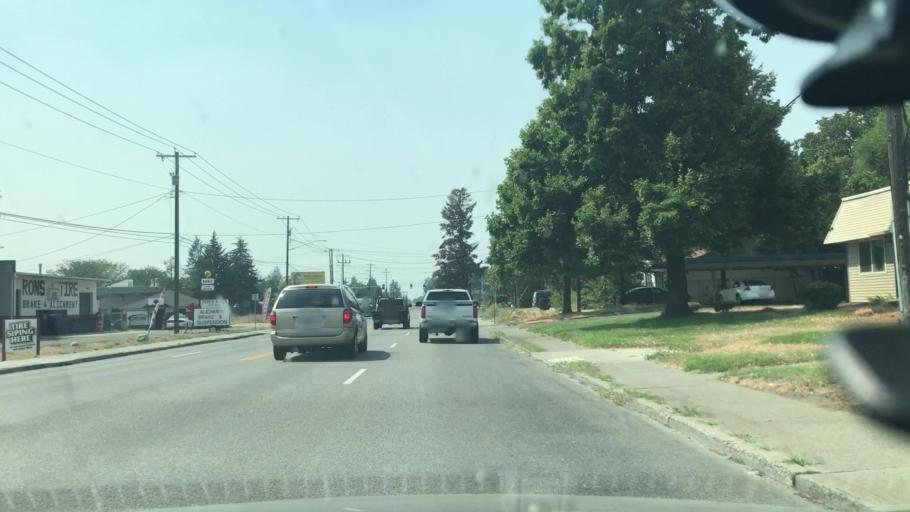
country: US
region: Washington
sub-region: Spokane County
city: Spokane
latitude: 47.6863
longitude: -117.3762
